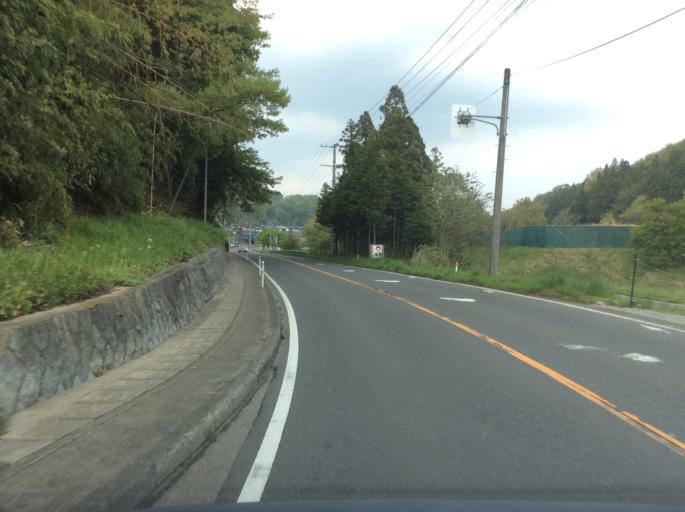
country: JP
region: Fukushima
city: Miharu
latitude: 37.4187
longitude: 140.4384
